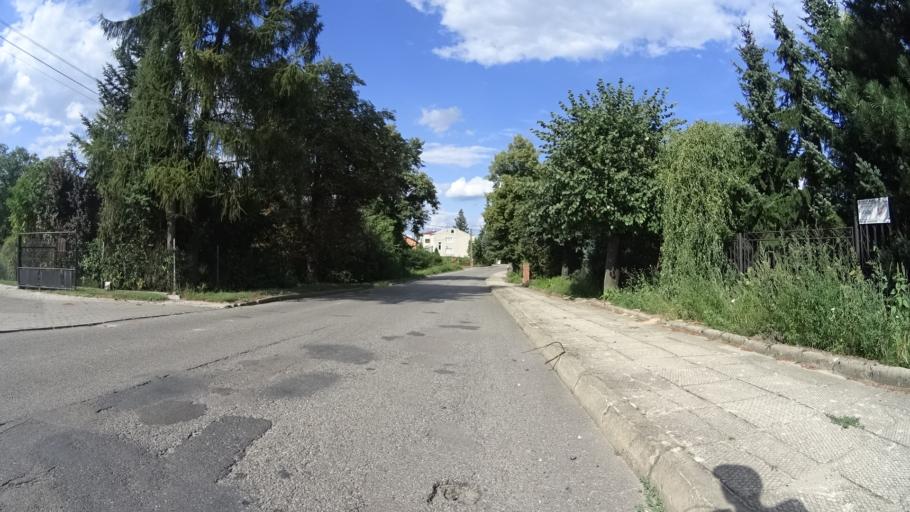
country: PL
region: Masovian Voivodeship
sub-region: Powiat grojecki
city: Mogielnica
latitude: 51.6872
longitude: 20.7191
